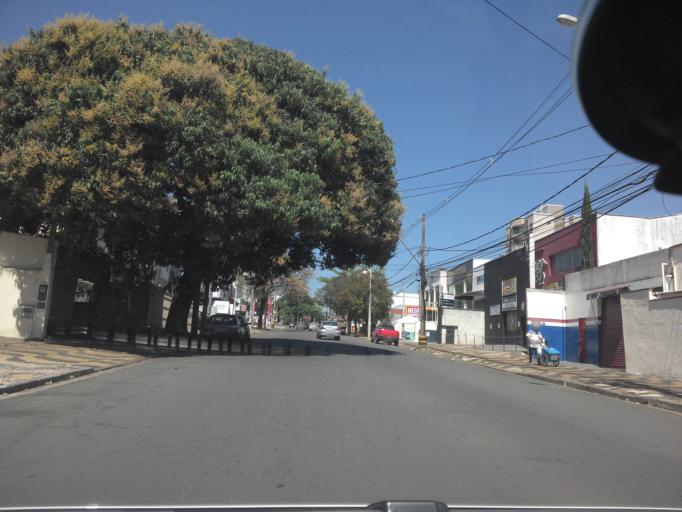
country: BR
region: Sao Paulo
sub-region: Campinas
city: Campinas
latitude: -22.8795
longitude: -47.0503
